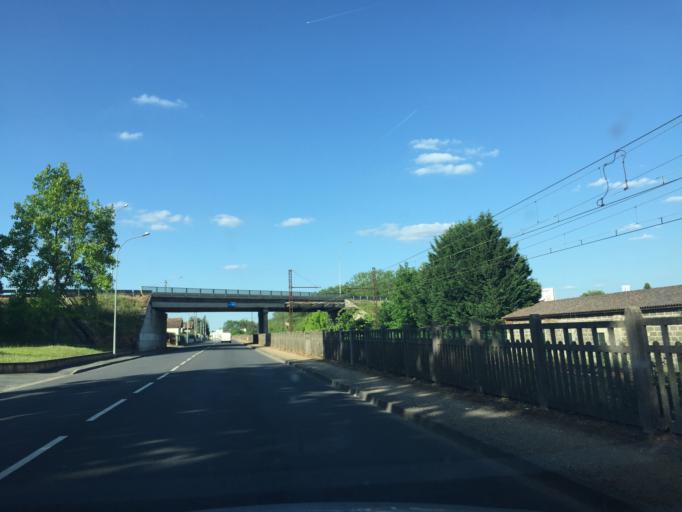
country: FR
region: Aquitaine
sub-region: Departement de la Gironde
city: Coutras
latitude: 45.0418
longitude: -0.1251
